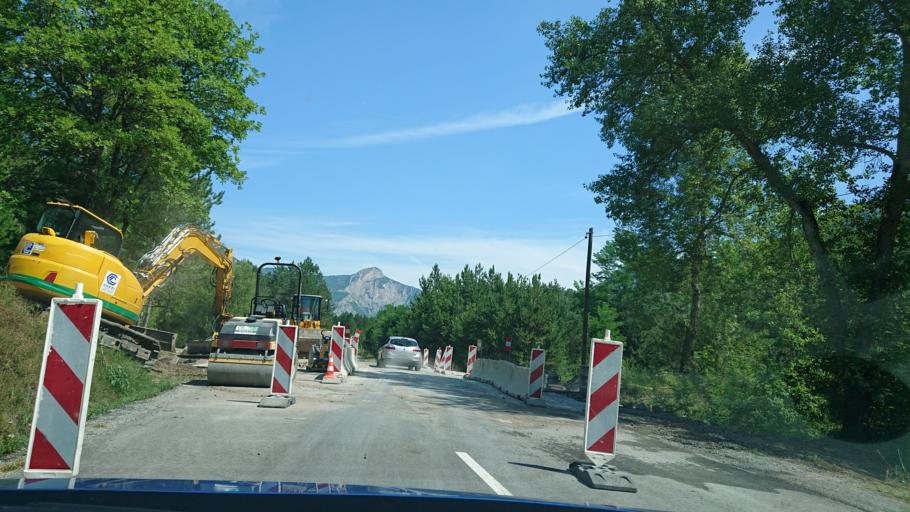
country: FR
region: Provence-Alpes-Cote d'Azur
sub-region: Departement des Hautes-Alpes
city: Tallard
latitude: 44.3208
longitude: 6.0301
